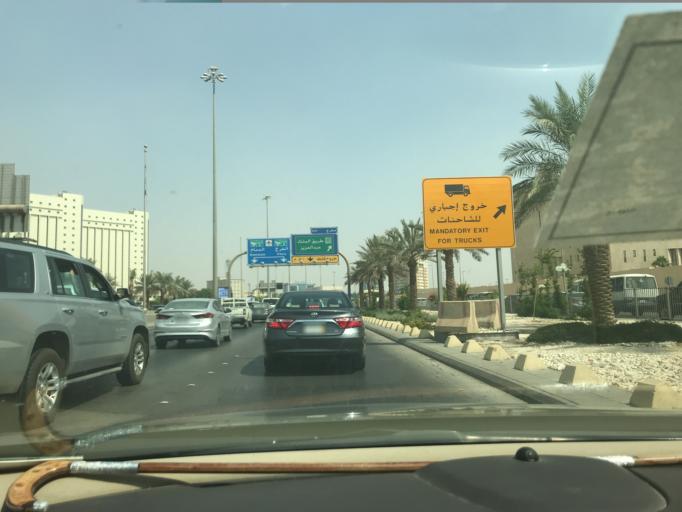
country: SA
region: Ar Riyad
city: Riyadh
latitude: 24.6862
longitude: 46.7065
